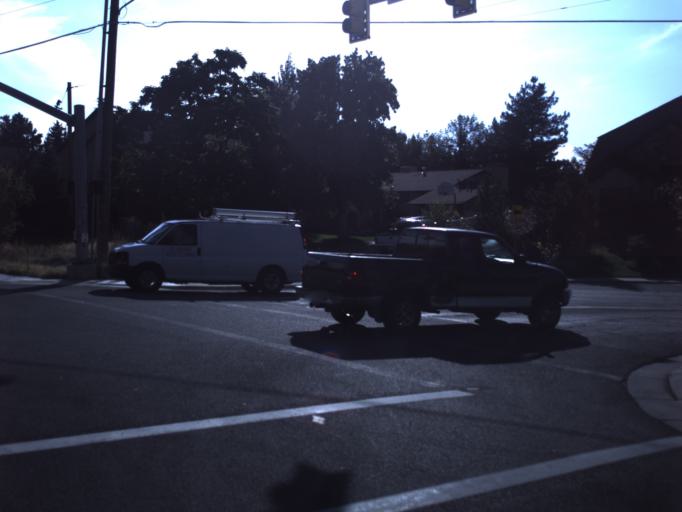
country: US
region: Utah
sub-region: Salt Lake County
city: Cottonwood Heights
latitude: 40.6031
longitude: -111.7956
